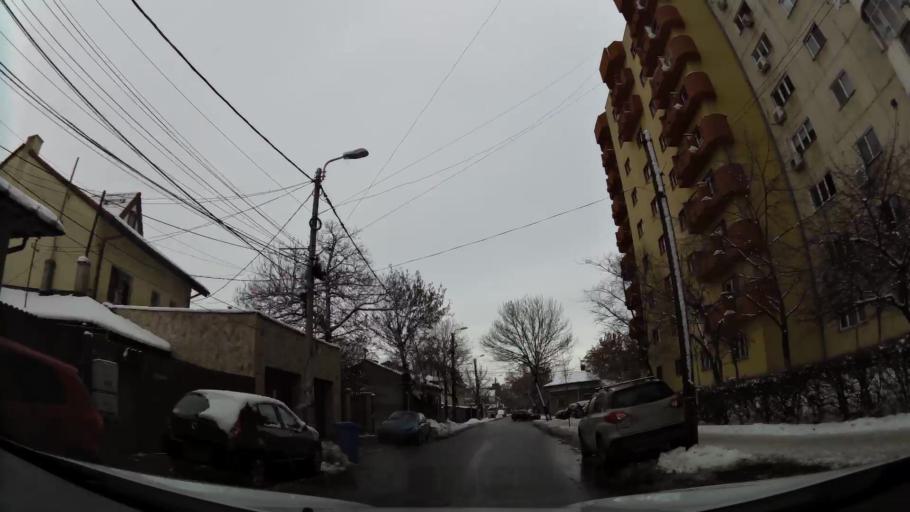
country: RO
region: Bucuresti
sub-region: Municipiul Bucuresti
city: Bucuresti
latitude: 44.3984
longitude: 26.1045
